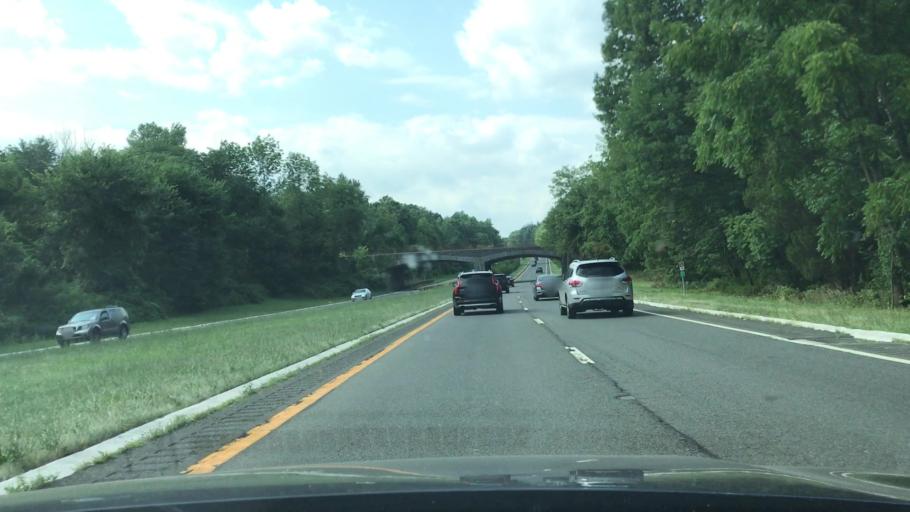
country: US
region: New York
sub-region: Rockland County
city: Blauvelt
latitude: 41.0681
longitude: -73.9798
